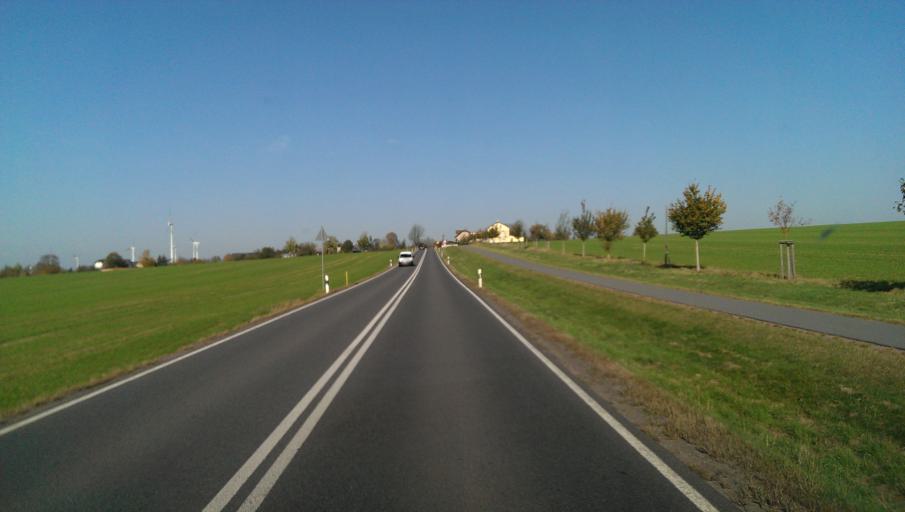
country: DE
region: Saxony
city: Erlau
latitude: 51.0046
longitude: 12.9494
